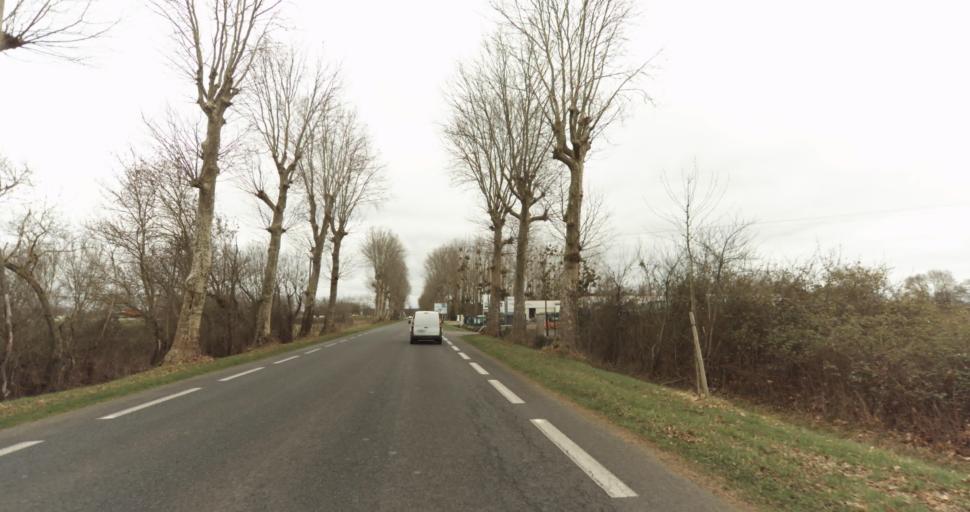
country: FR
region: Pays de la Loire
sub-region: Departement de Maine-et-Loire
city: Villebernier
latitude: 47.2837
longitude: -0.0509
